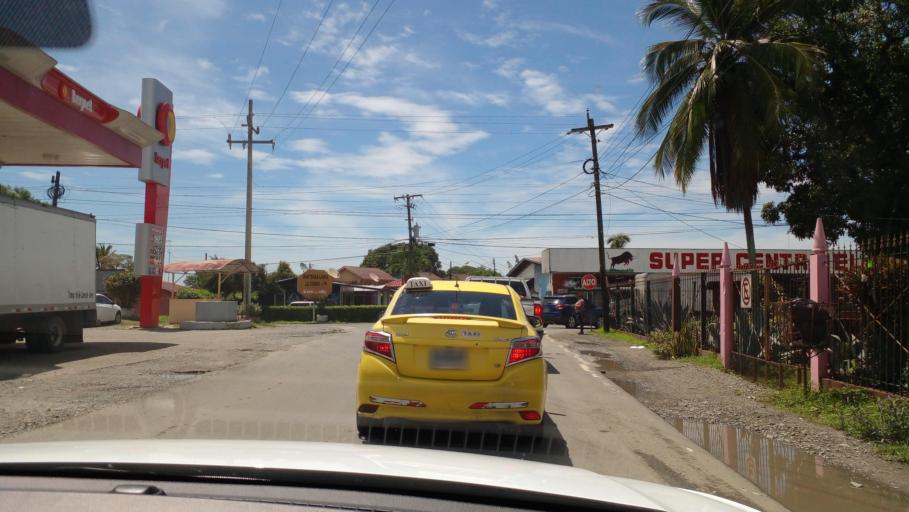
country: PA
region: Bocas del Toro
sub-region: Distrito de Changuinola
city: Changuinola
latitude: 9.4153
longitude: -82.5228
